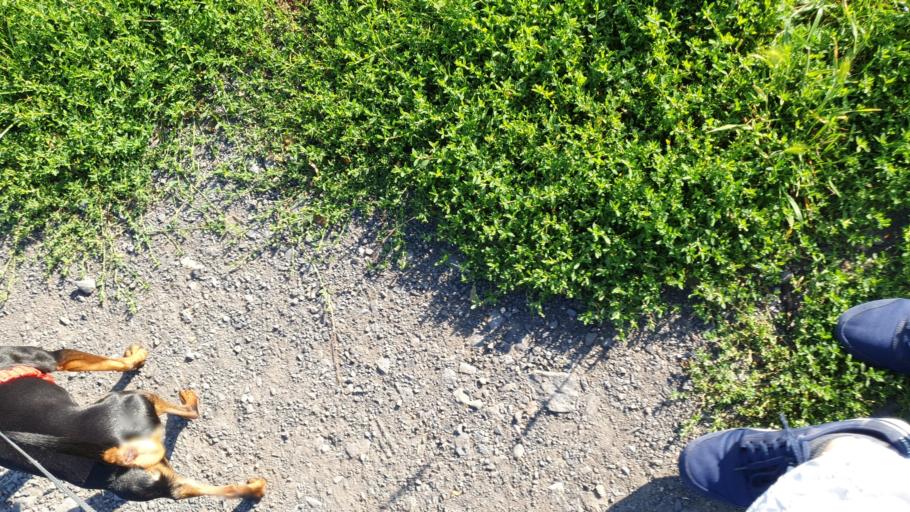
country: FR
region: Auvergne
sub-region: Departement du Puy-de-Dome
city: Aydat
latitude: 45.5740
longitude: 3.0138
